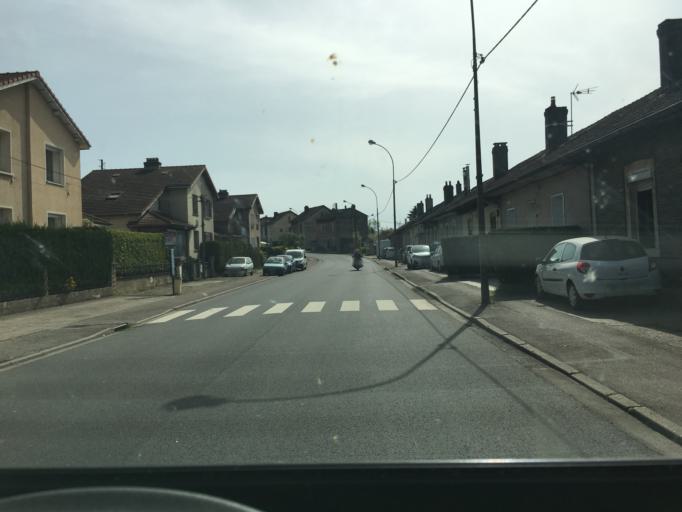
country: FR
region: Lorraine
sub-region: Departement de Meurthe-et-Moselle
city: Neuves-Maisons
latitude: 48.6136
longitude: 6.1183
